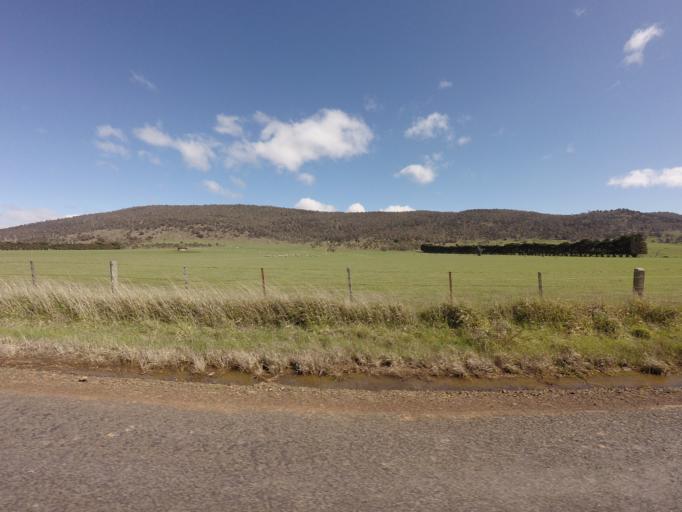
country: AU
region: Tasmania
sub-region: Northern Midlands
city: Evandale
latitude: -41.9634
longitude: 147.4396
